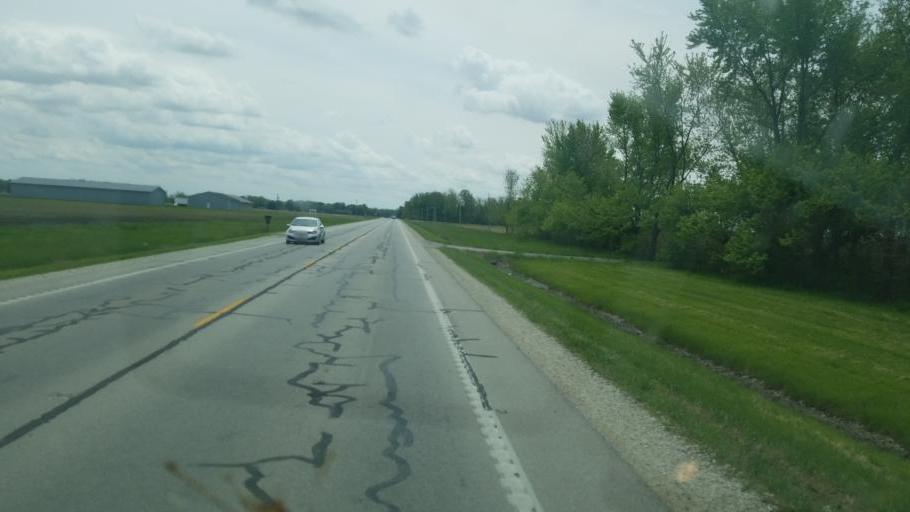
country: US
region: Ohio
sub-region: Sandusky County
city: Ballville
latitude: 41.3097
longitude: -83.1685
